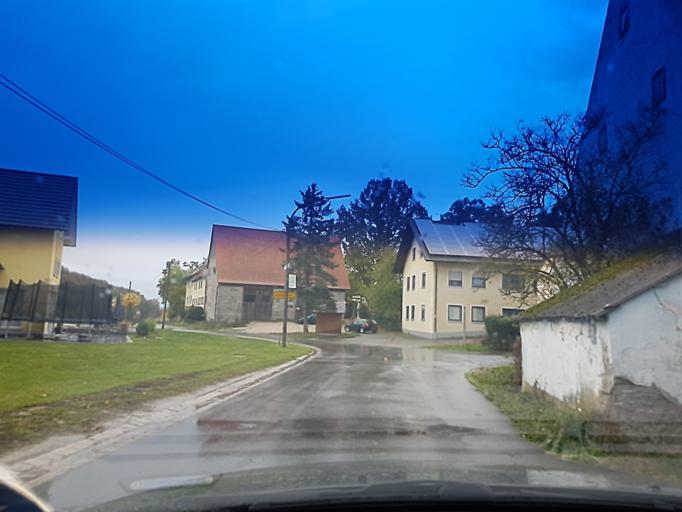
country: DE
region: Bavaria
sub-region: Regierungsbezirk Mittelfranken
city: Wachenroth
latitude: 49.7585
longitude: 10.6915
